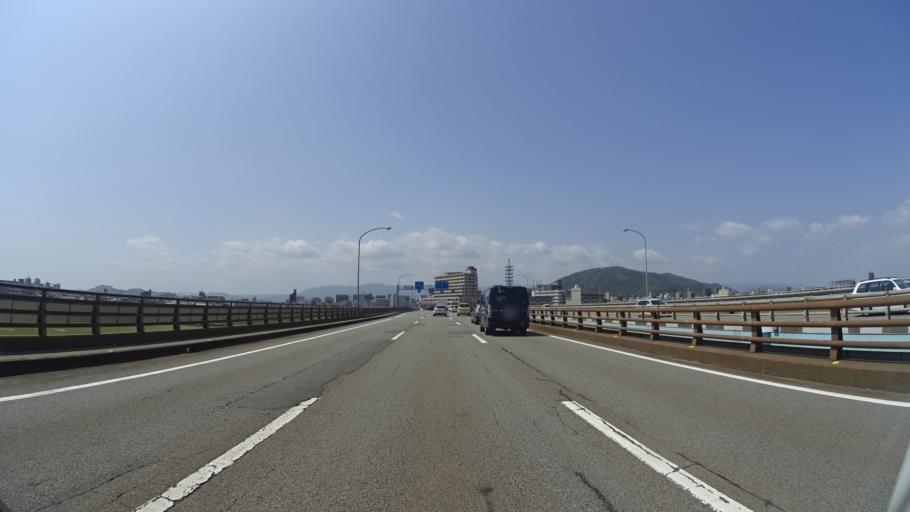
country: JP
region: Tokushima
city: Tokushima-shi
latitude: 34.0868
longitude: 134.5662
